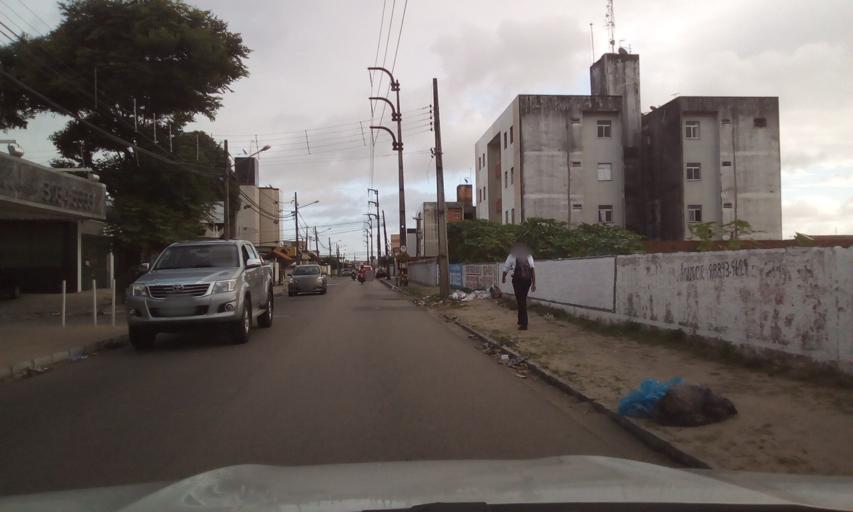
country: BR
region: Paraiba
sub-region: Joao Pessoa
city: Joao Pessoa
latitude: -7.1679
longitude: -34.8597
